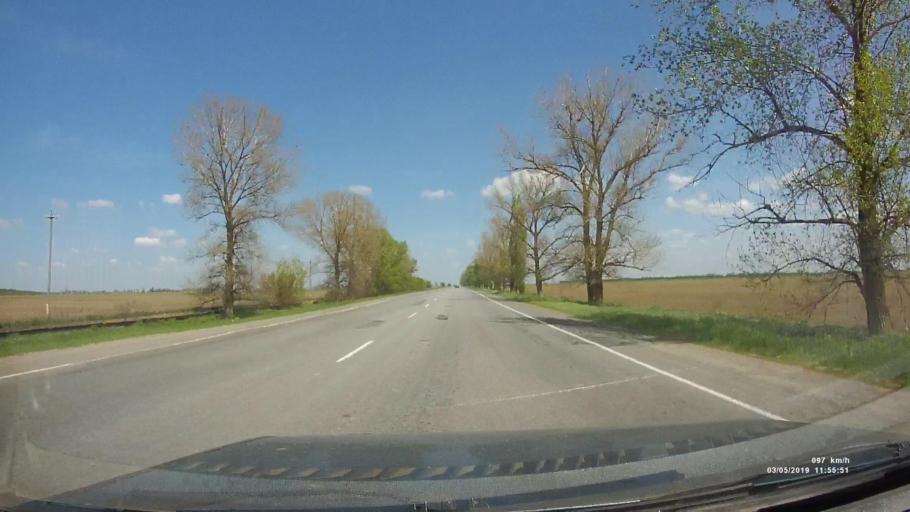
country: RU
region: Rostov
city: Bagayevskaya
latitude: 47.1865
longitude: 40.2951
